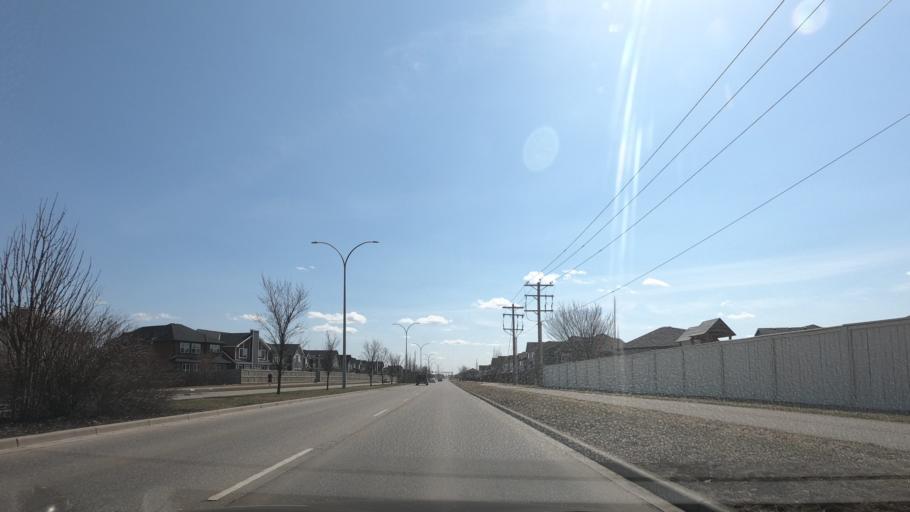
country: CA
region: Alberta
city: Airdrie
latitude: 51.2633
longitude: -114.0256
